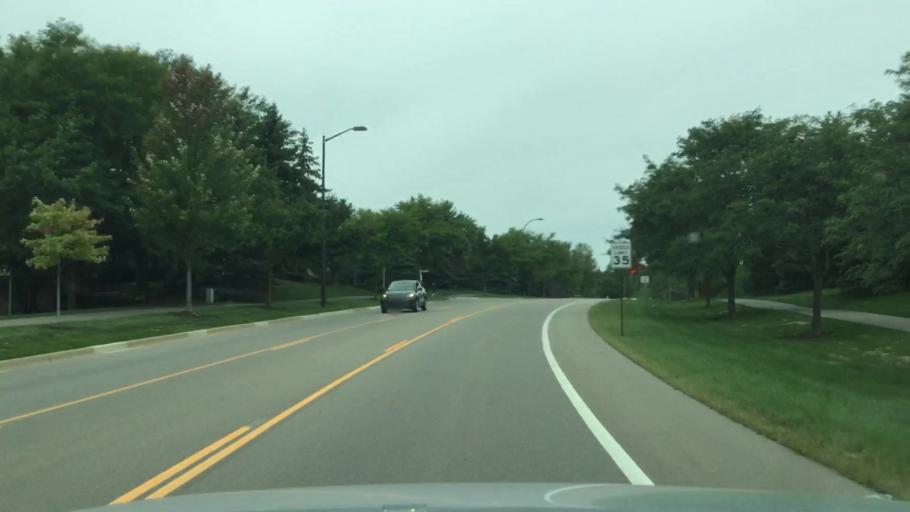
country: US
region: Michigan
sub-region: Washtenaw County
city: Ann Arbor
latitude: 42.3165
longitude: -83.7044
